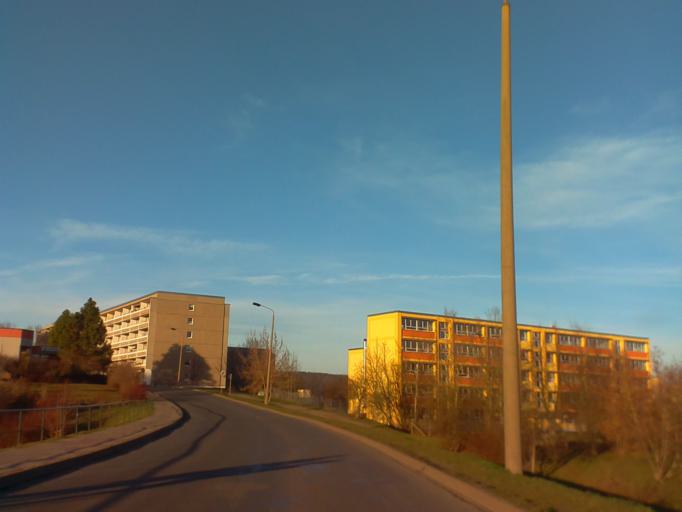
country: DE
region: Thuringia
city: Rudolstadt
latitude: 50.6968
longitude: 11.3205
